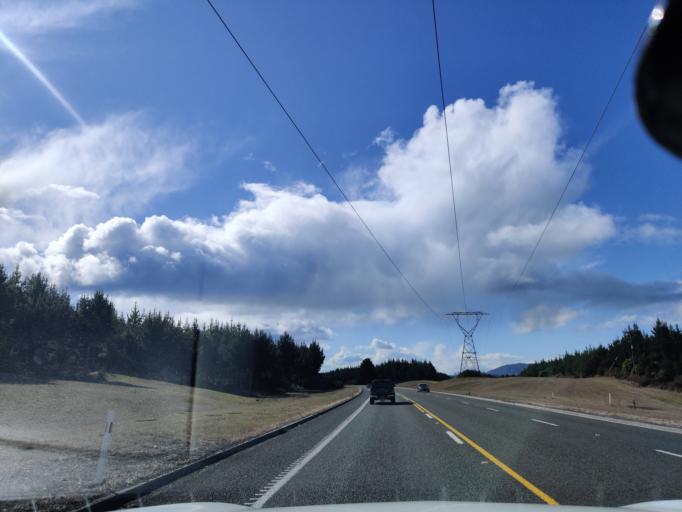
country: NZ
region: Waikato
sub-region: Taupo District
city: Taupo
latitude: -38.8108
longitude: 176.0790
